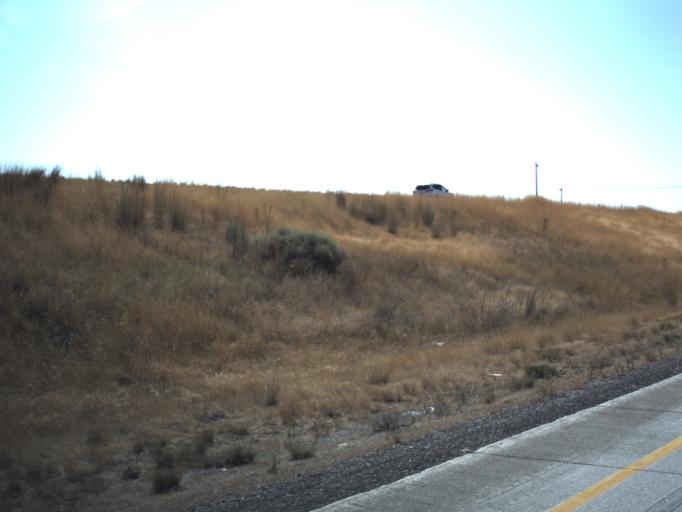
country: US
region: Utah
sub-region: Salt Lake County
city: Salt Lake City
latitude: 40.7867
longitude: -111.9497
